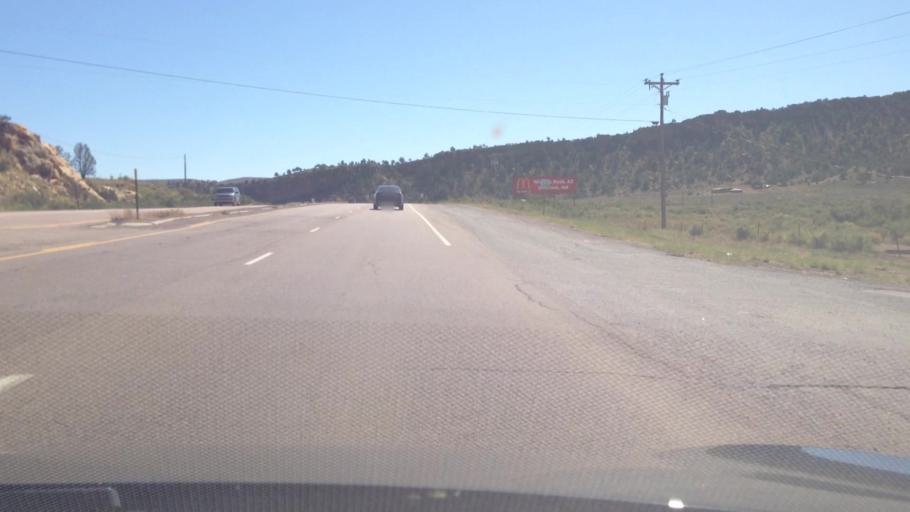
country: US
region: Arizona
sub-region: Apache County
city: Window Rock
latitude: 35.6557
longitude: -109.0396
